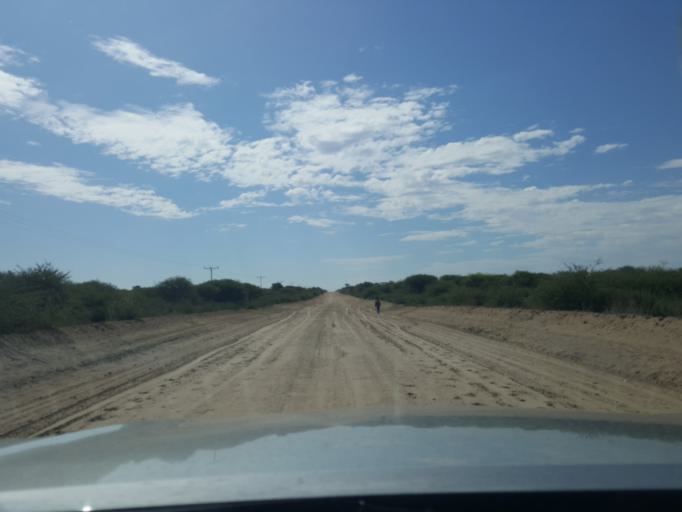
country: BW
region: Kweneng
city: Khudumelapye
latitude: -23.8791
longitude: 24.9055
